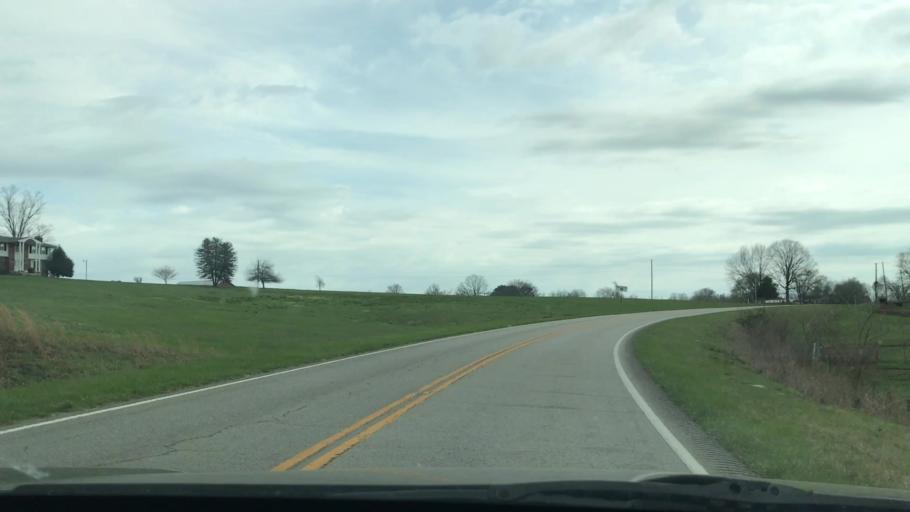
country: US
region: Kentucky
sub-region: Hart County
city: Munfordville
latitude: 37.2985
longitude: -85.7629
